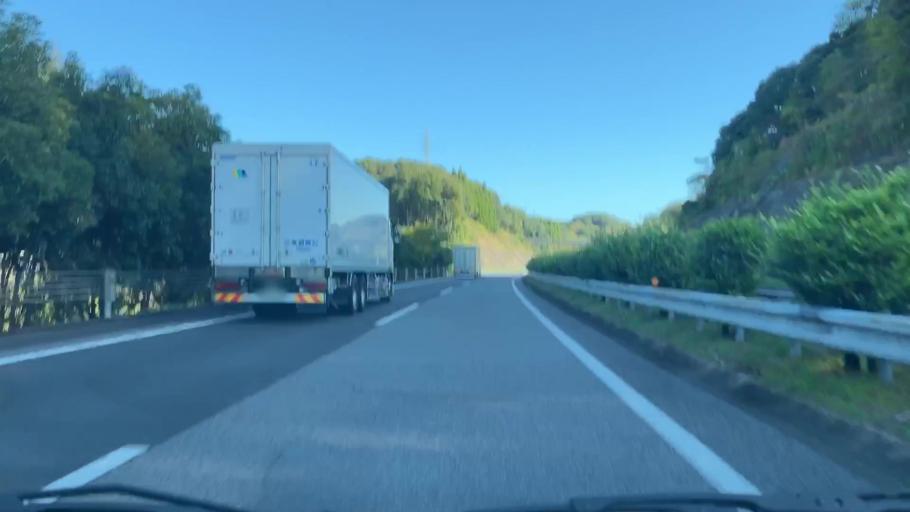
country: JP
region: Saga Prefecture
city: Takeocho-takeo
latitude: 33.2280
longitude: 130.0518
